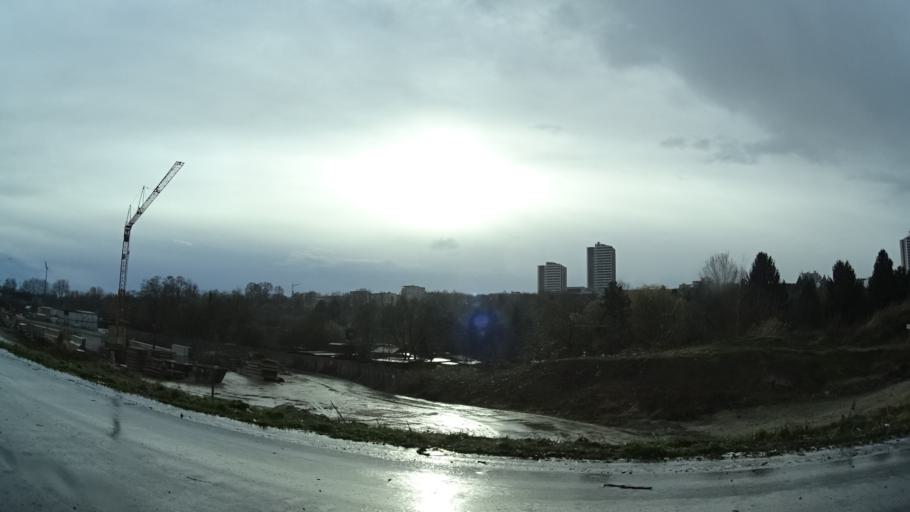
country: DE
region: Hesse
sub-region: Regierungsbezirk Darmstadt
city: Frankfurt am Main
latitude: 50.1333
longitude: 8.7243
